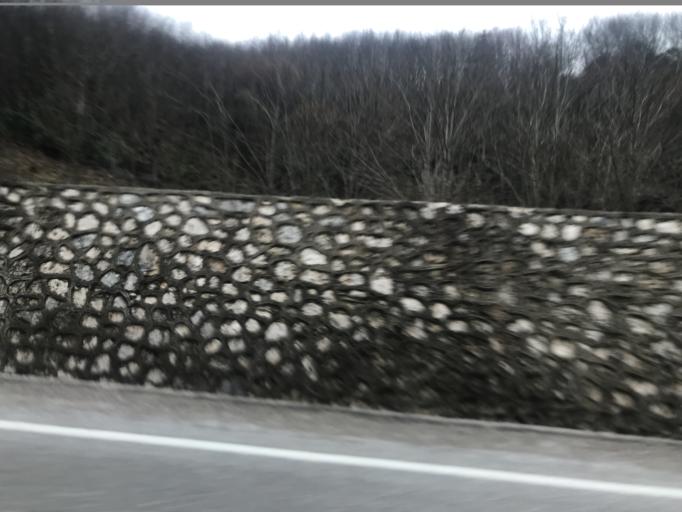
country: TR
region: Bartin
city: Amasra
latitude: 41.7039
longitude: 32.3852
